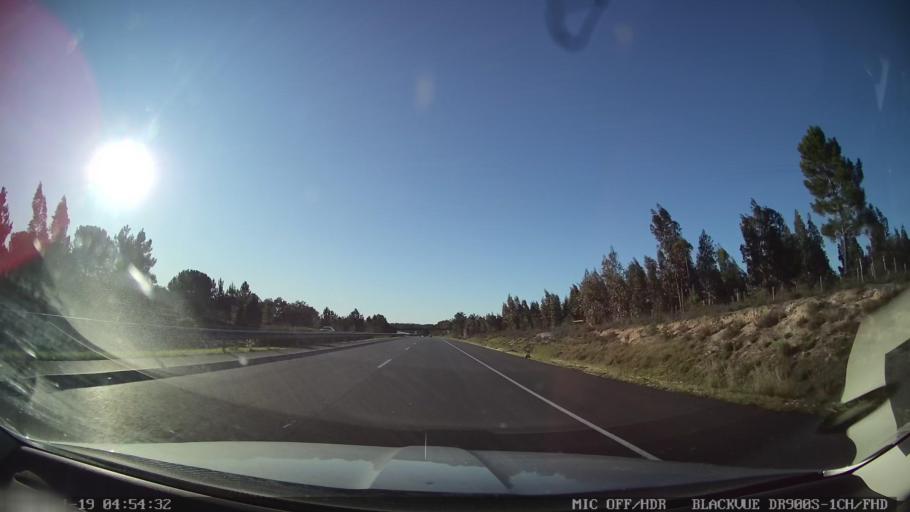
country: PT
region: Evora
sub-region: Vendas Novas
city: Vendas Novas
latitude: 38.6397
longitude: -8.4871
